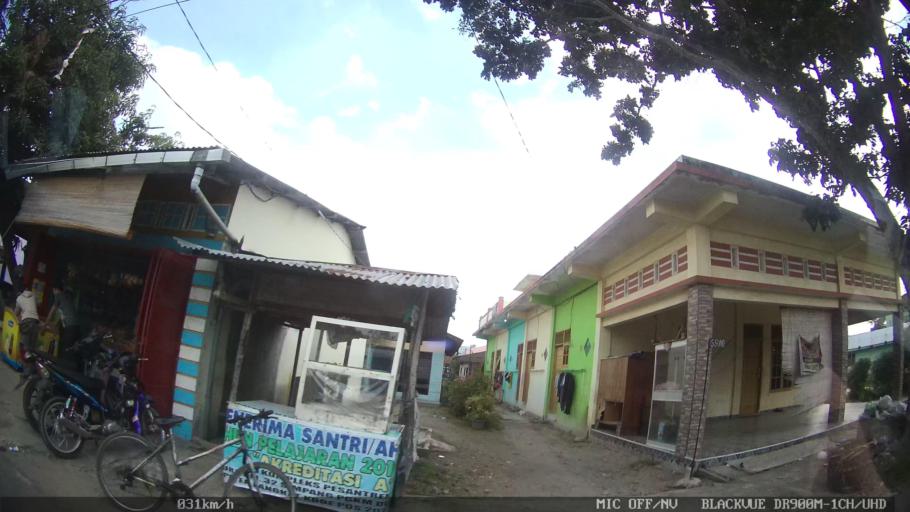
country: ID
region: North Sumatra
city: Binjai
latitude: 3.6353
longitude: 98.5097
